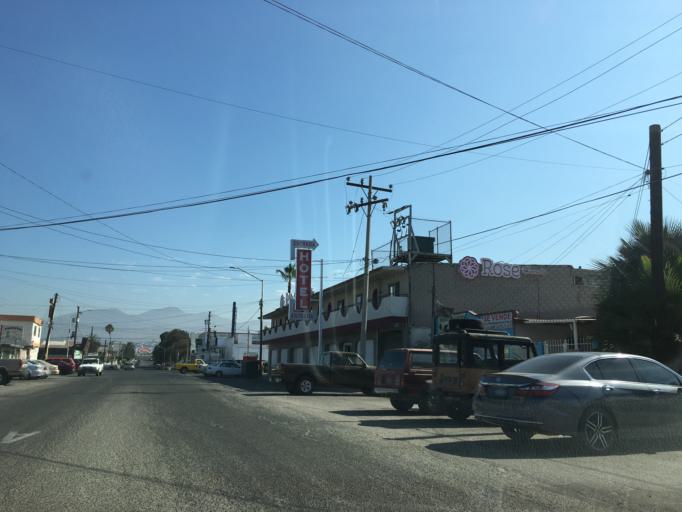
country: MX
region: Baja California
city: Ensenada
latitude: 31.8618
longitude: -116.6129
